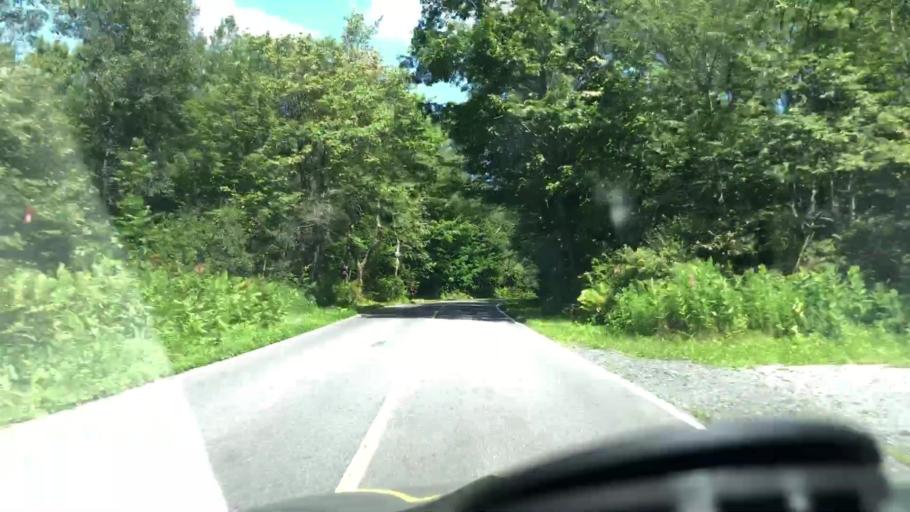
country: US
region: Massachusetts
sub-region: Berkshire County
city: Lanesborough
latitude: 42.5839
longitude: -73.2020
